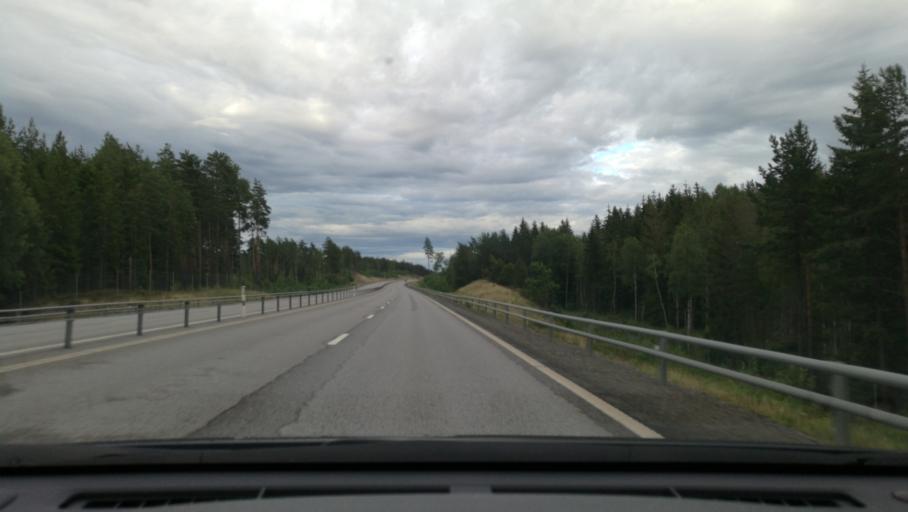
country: SE
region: OEstergoetland
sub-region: Norrkopings Kommun
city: Svartinge
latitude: 58.6682
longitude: 16.0032
